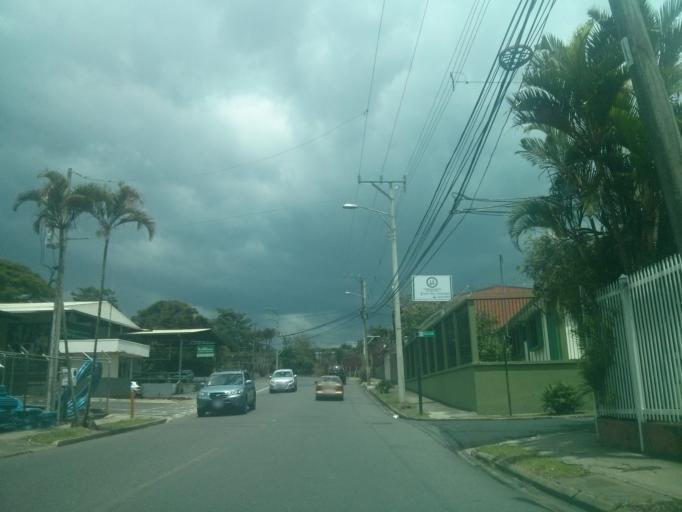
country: CR
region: San Jose
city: San Pedro
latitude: 9.9251
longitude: -84.0671
